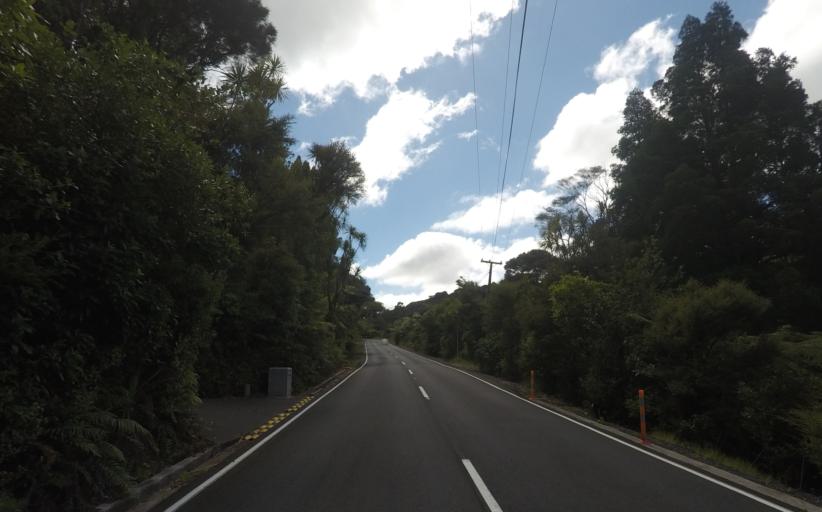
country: NZ
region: Auckland
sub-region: Auckland
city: Muriwai Beach
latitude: -36.8647
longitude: 174.5119
